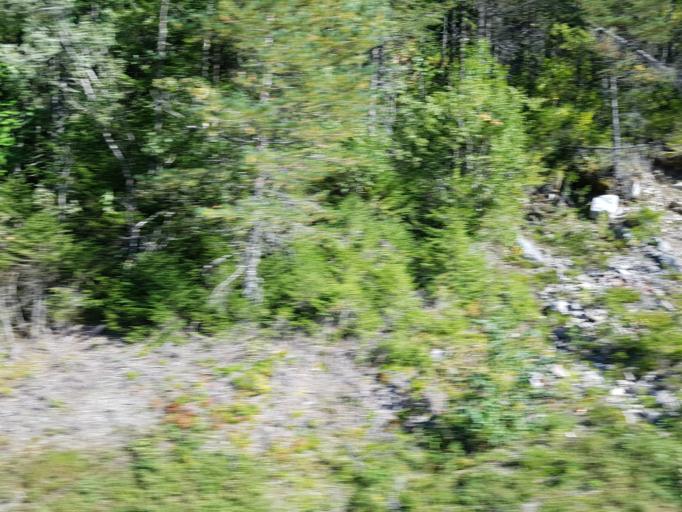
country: NO
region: Sor-Trondelag
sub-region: Afjord
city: A i Afjord
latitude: 63.7403
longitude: 10.2363
